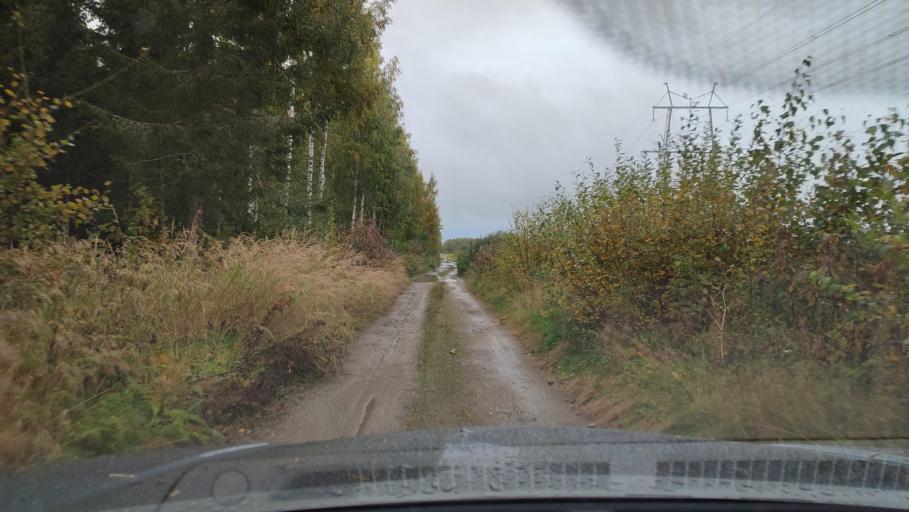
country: FI
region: Southern Ostrobothnia
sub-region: Suupohja
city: Karijoki
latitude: 62.2221
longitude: 21.6268
